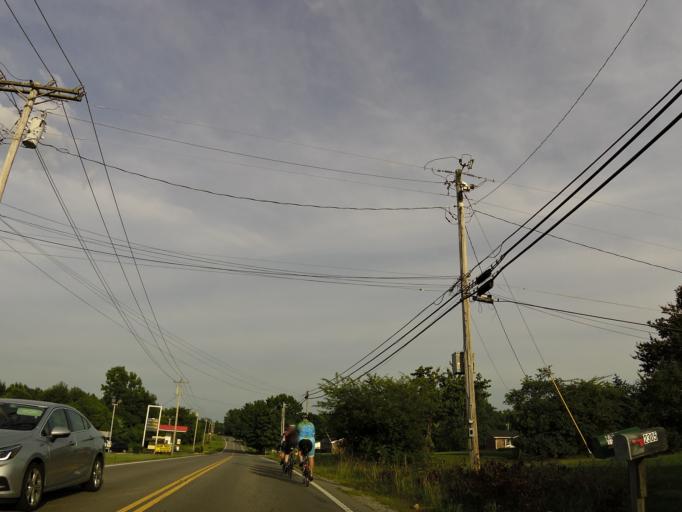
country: US
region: Tennessee
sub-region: Dickson County
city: Burns
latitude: 36.0583
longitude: -87.3355
